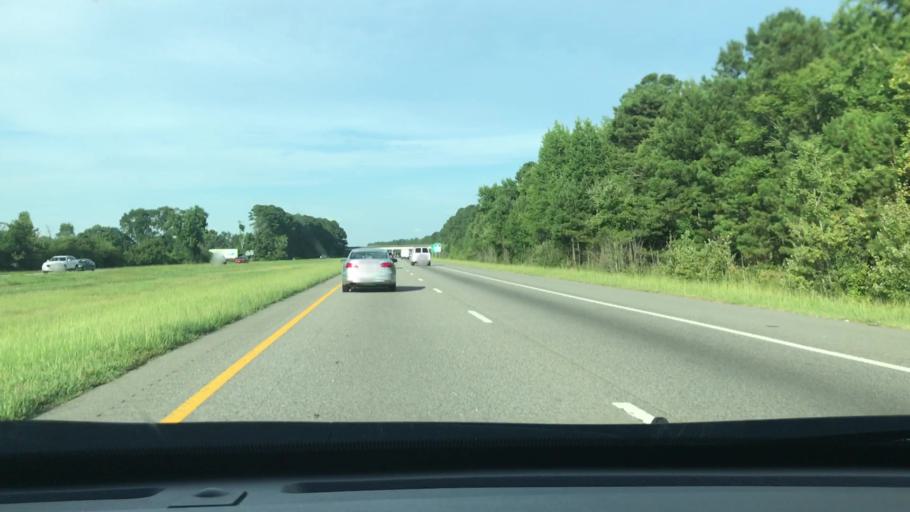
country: US
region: North Carolina
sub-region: Robeson County
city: Fairmont
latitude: 34.5851
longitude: -79.1316
